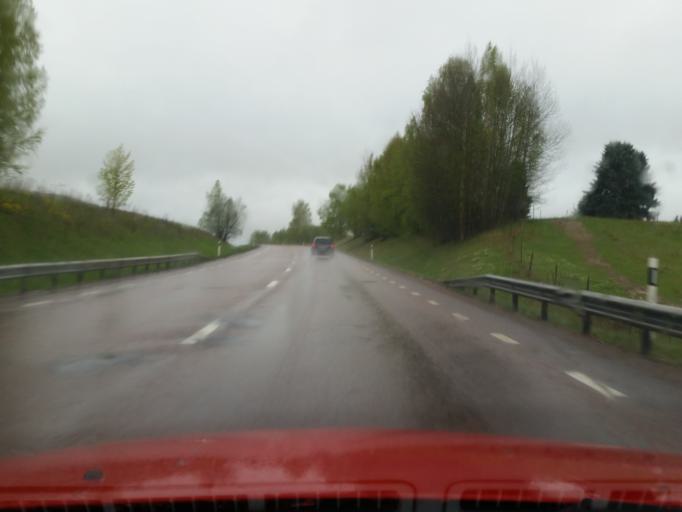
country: SE
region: Dalarna
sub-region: Borlange Kommun
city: Borlaenge
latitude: 60.4548
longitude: 15.4798
